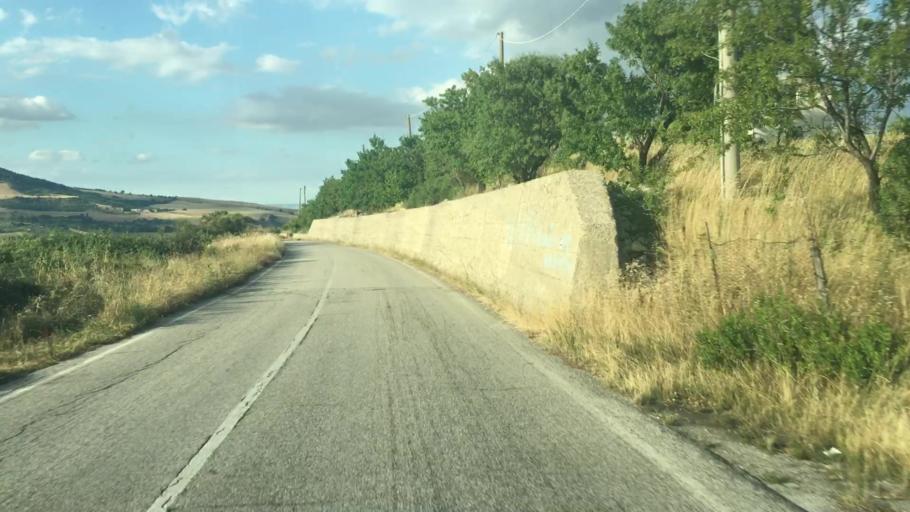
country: IT
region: Basilicate
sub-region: Provincia di Potenza
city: Tolve
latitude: 40.6958
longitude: 15.9924
